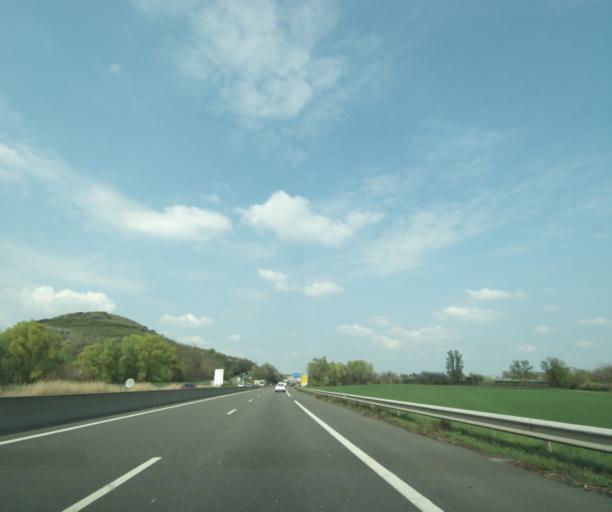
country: FR
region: Auvergne
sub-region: Departement du Puy-de-Dome
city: Aubiere
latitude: 45.7679
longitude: 3.1389
